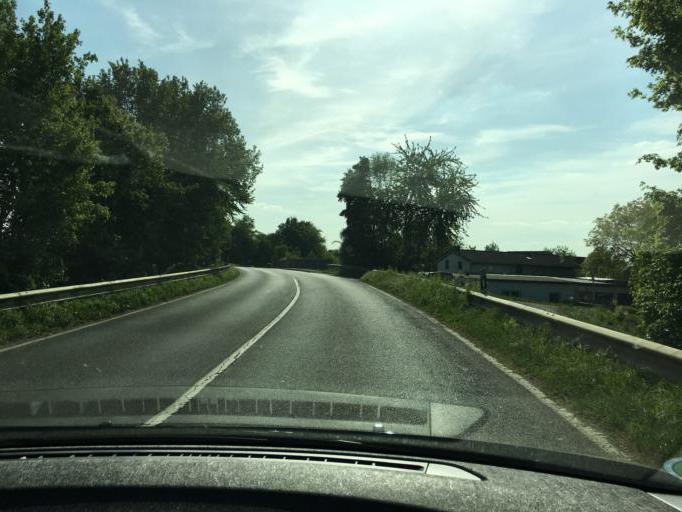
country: DE
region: North Rhine-Westphalia
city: Wesseling
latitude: 50.7924
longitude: 6.9639
